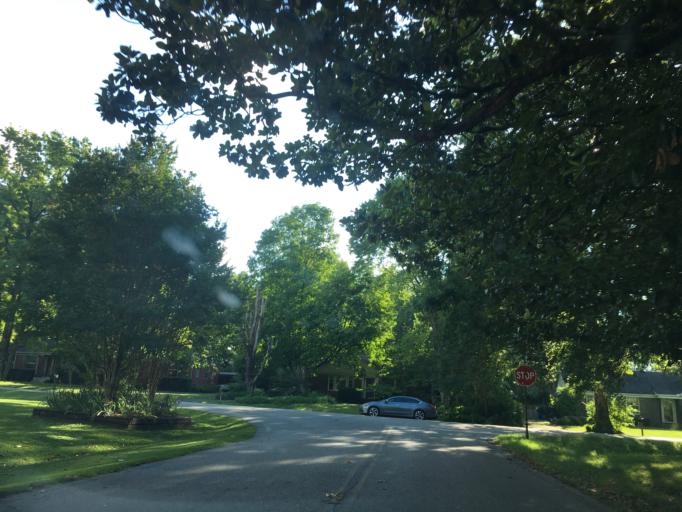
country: US
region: Tennessee
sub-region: Davidson County
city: Oak Hill
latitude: 36.1063
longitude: -86.7763
